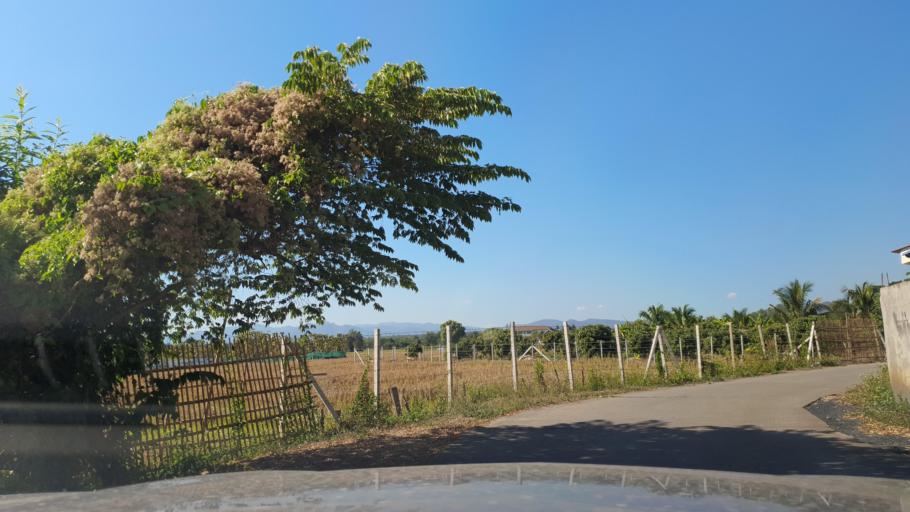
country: TH
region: Chiang Mai
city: San Pa Tong
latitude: 18.6472
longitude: 98.8681
